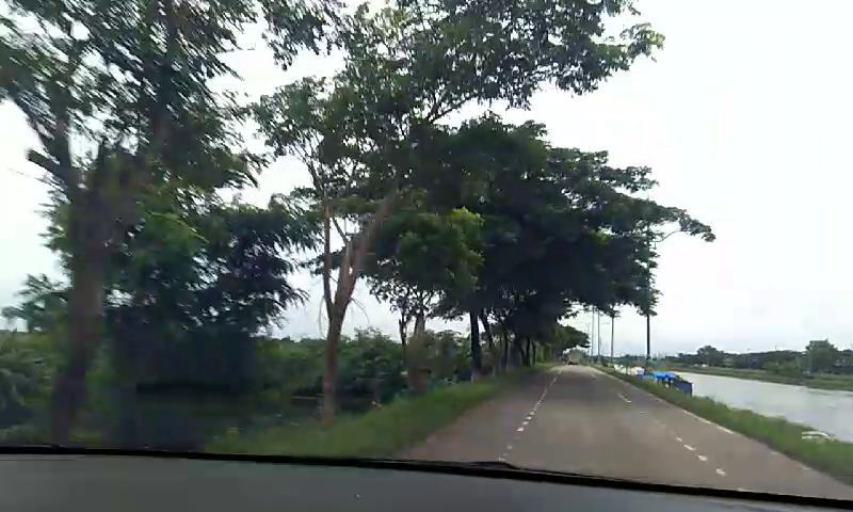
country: ID
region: West Java
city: Bekasi
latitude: -6.1286
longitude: 106.9691
